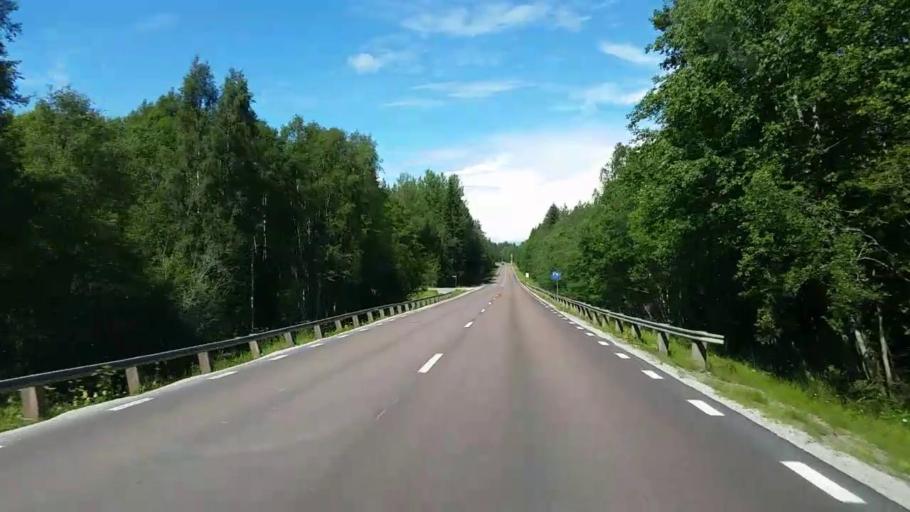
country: SE
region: Dalarna
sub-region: Rattviks Kommun
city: Raettvik
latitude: 61.0299
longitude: 15.2068
